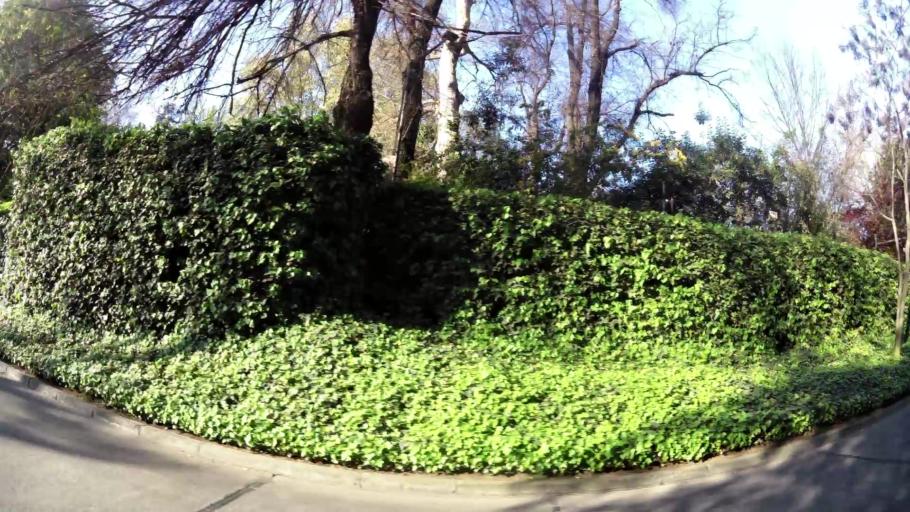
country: CL
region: Santiago Metropolitan
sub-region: Provincia de Santiago
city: Villa Presidente Frei, Nunoa, Santiago, Chile
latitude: -33.3874
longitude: -70.5258
